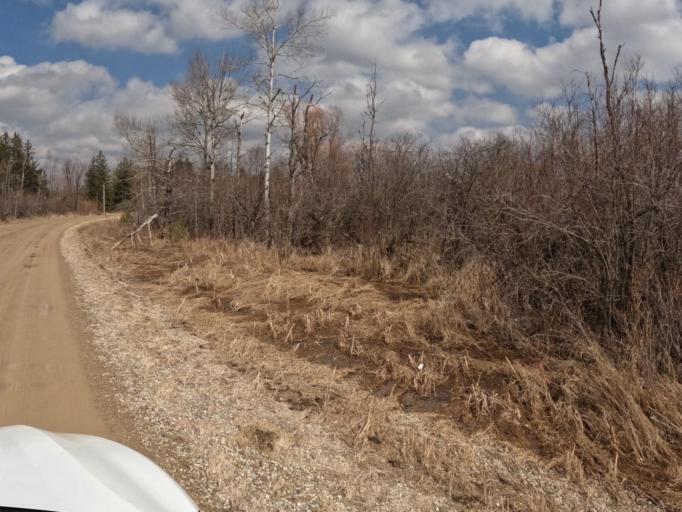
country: CA
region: Ontario
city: Shelburne
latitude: 44.0322
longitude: -80.2365
